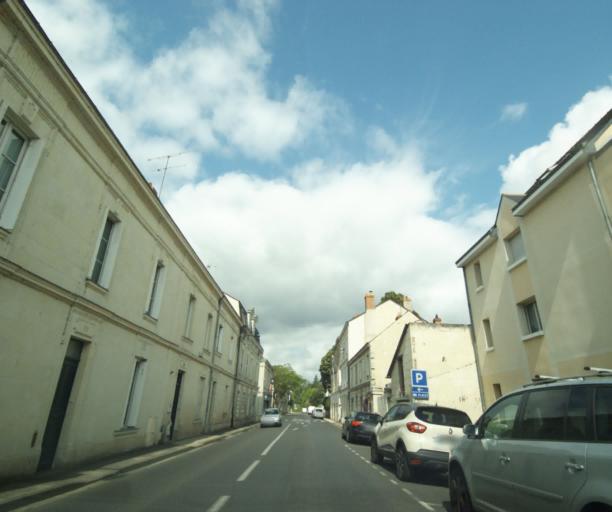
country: FR
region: Pays de la Loire
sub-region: Departement de Maine-et-Loire
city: Saumur
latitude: 47.2648
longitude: -0.0984
